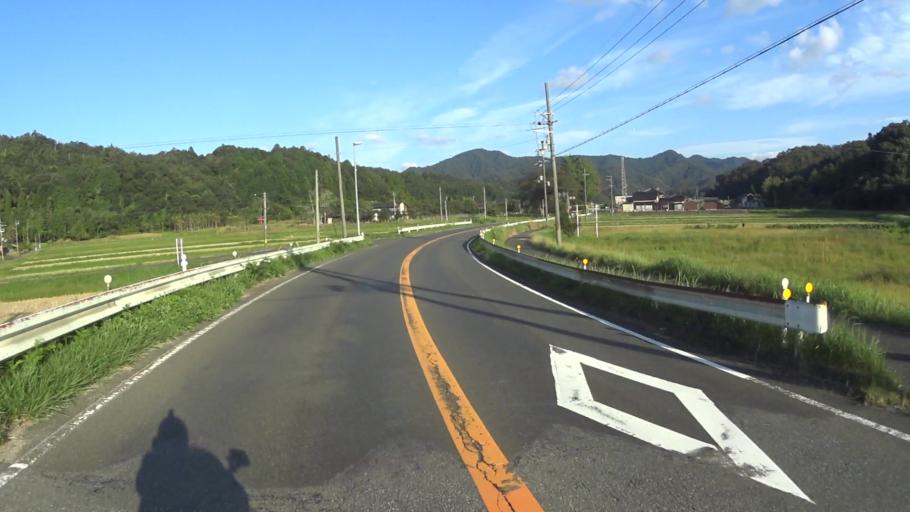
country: JP
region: Hyogo
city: Toyooka
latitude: 35.5804
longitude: 134.9687
